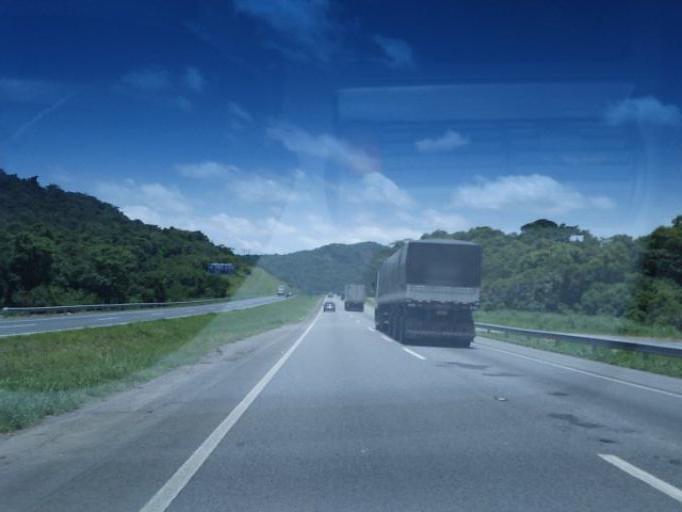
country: BR
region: Sao Paulo
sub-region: Juquia
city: Juquia
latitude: -24.3513
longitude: -47.6558
